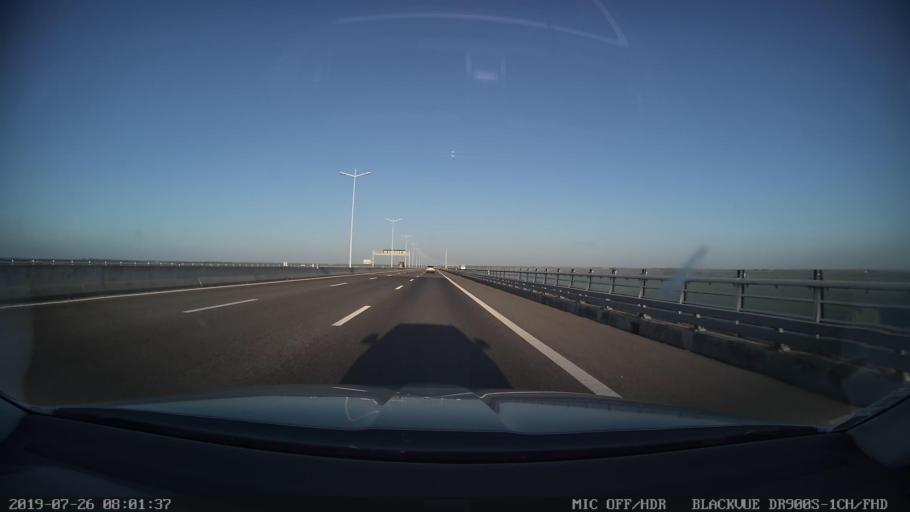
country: PT
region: Lisbon
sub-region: Vila Franca de Xira
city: Castanheira do Ribatejo
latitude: 39.0114
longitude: -8.9296
